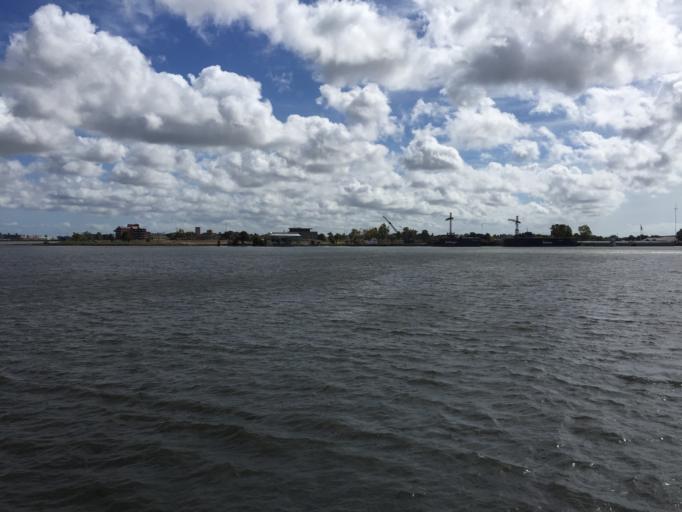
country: US
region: Louisiana
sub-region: Orleans Parish
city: New Orleans
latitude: 29.9541
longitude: -90.0625
